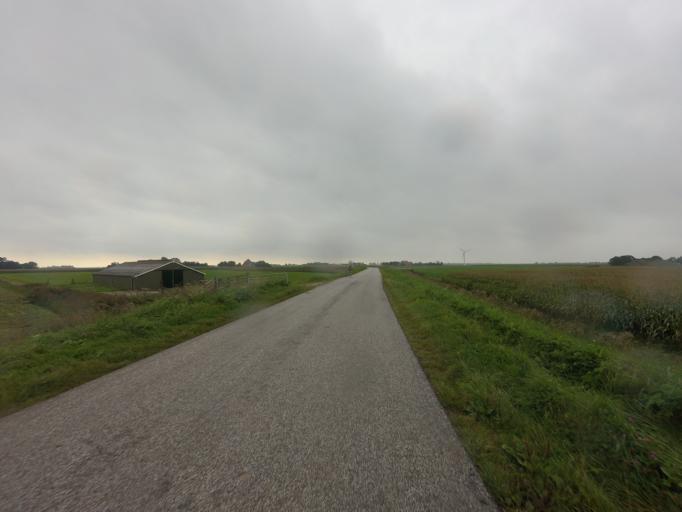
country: NL
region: Friesland
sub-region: Sudwest Fryslan
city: Workum
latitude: 52.9682
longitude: 5.4329
